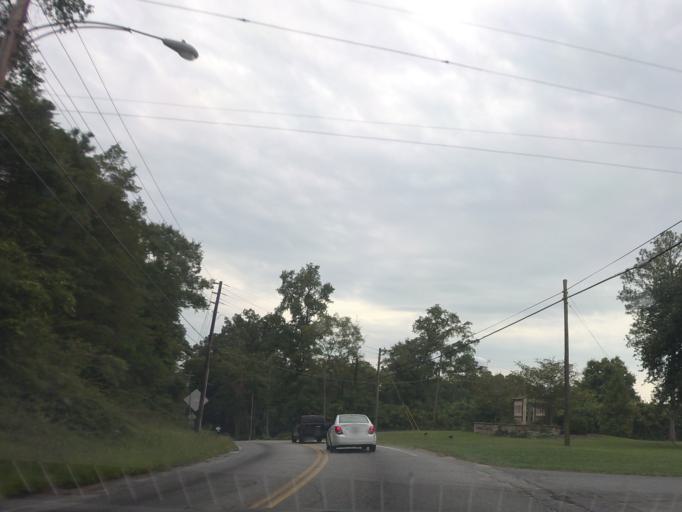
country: US
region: Georgia
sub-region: Bibb County
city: Macon
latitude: 32.8682
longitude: -83.6901
